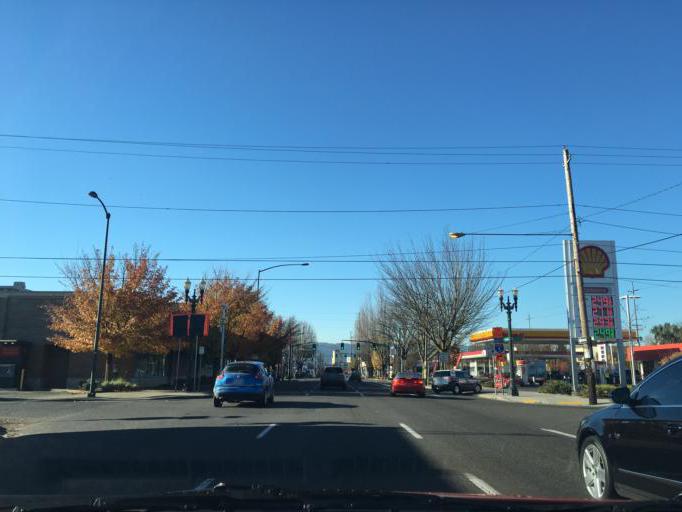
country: US
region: Oregon
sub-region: Multnomah County
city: Portland
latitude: 45.5351
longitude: -122.6592
